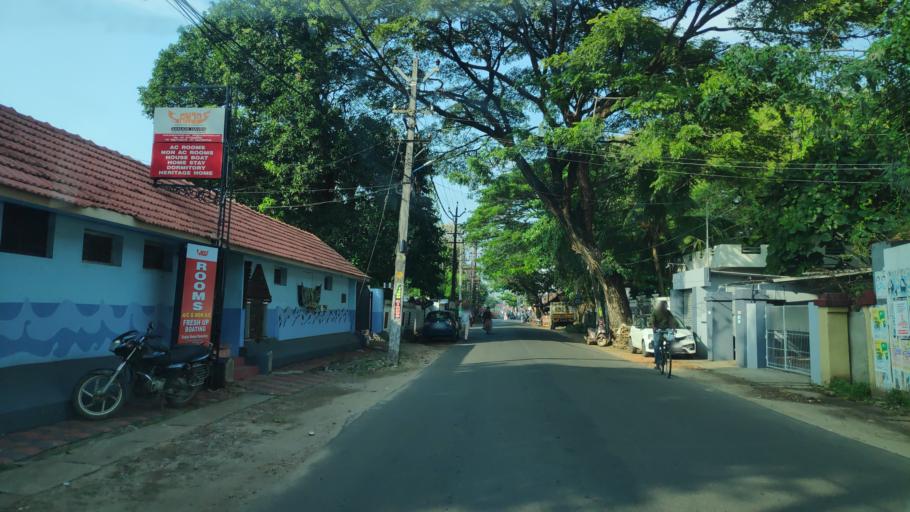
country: IN
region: Kerala
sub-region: Alappuzha
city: Alleppey
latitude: 9.4908
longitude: 76.3336
